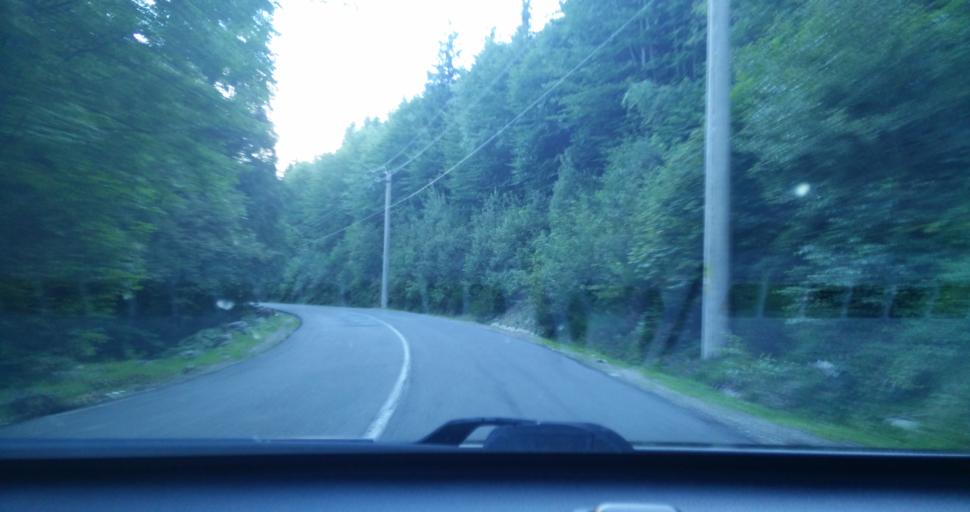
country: RO
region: Bihor
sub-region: Oras Nucet
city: Nucet
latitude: 46.5174
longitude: 22.6464
